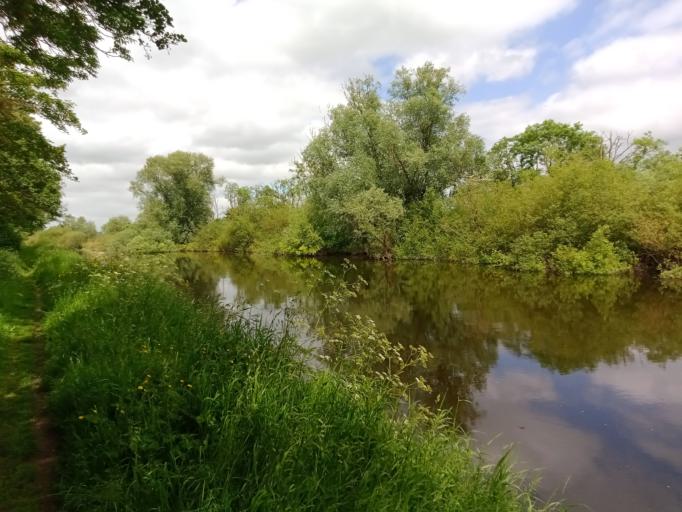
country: IE
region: Leinster
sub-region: County Carlow
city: Carlow
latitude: 52.7988
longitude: -6.9623
